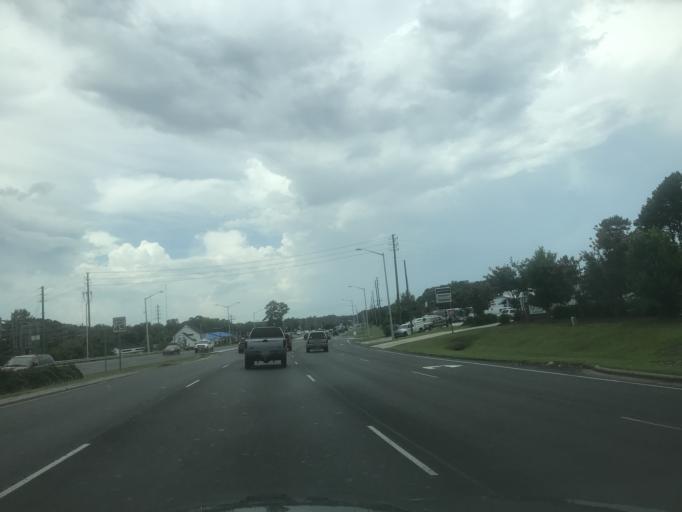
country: US
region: North Carolina
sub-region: Johnston County
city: Clayton
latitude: 35.6469
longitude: -78.4655
